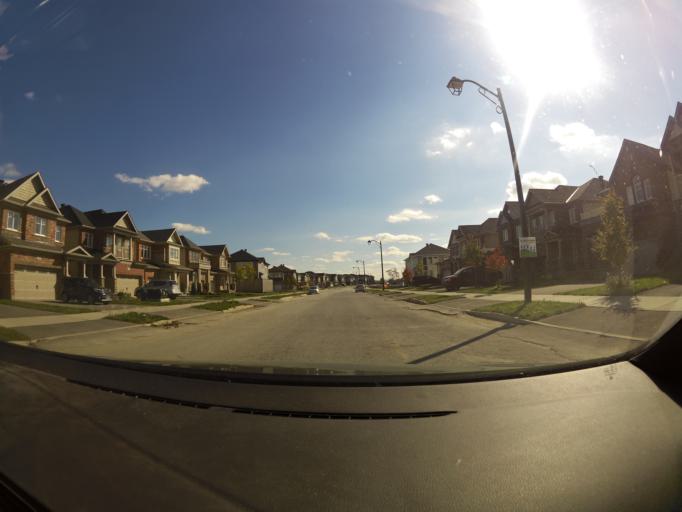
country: CA
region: Ontario
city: Bells Corners
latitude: 45.2777
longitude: -75.8827
